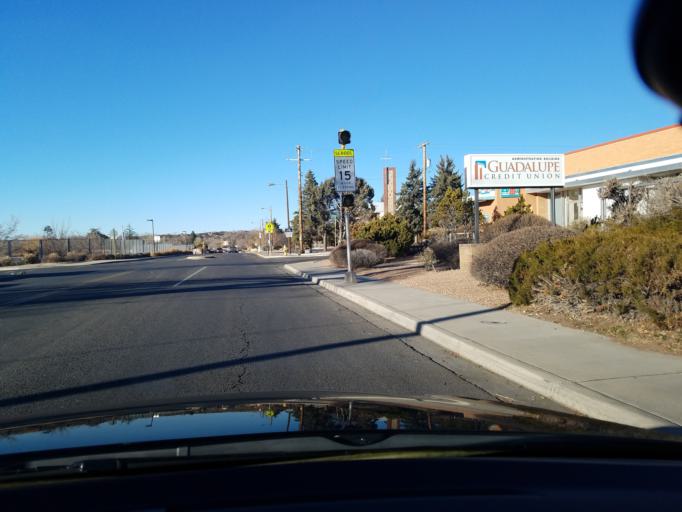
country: US
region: New Mexico
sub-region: Santa Fe County
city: Agua Fria
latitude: 35.6635
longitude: -105.9775
